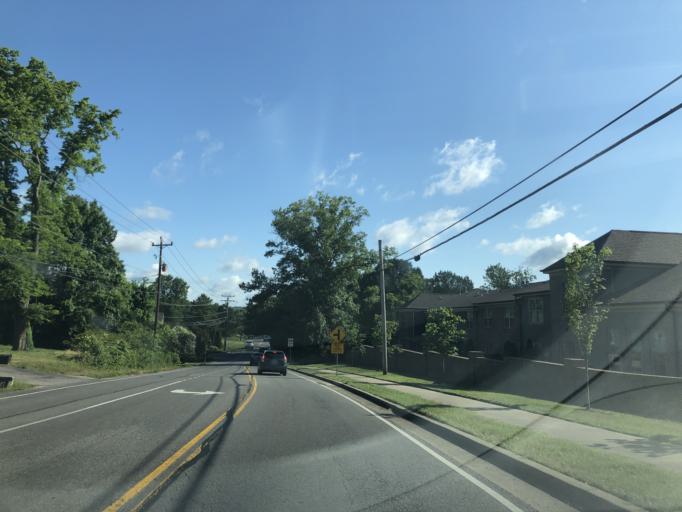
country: US
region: Tennessee
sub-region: Davidson County
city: Belle Meade
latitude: 36.0487
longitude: -86.9528
